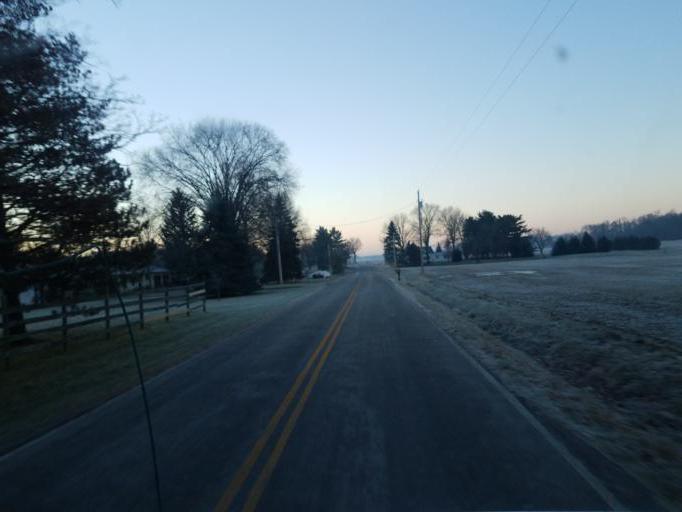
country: US
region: Ohio
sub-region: Marion County
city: Marion
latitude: 40.5373
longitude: -83.0242
